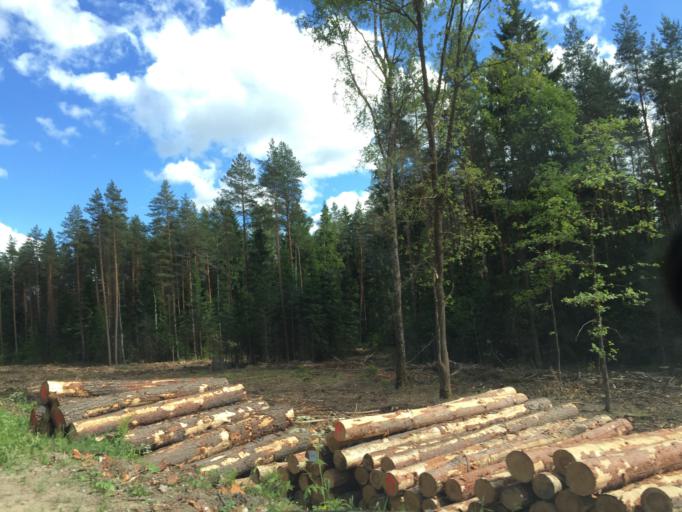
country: LV
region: Vecumnieki
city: Vecumnieki
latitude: 56.4222
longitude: 24.5108
